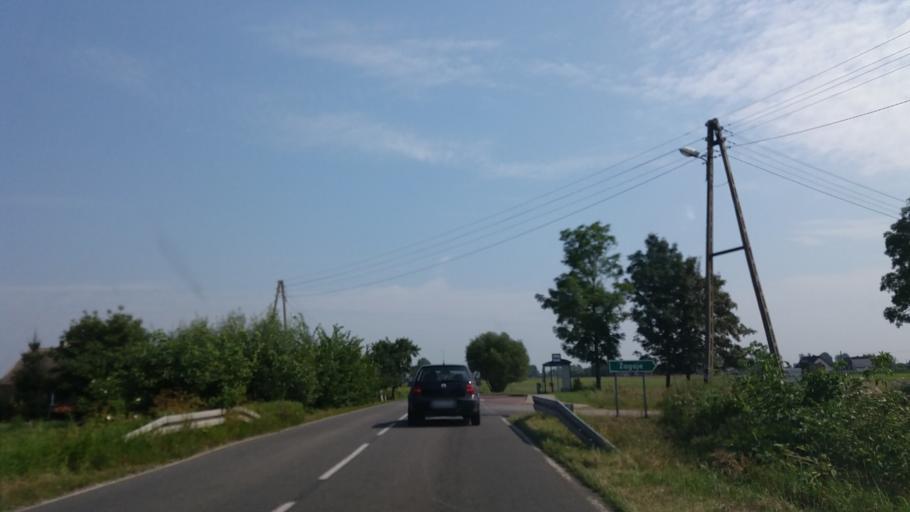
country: PL
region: Lubusz
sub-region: Powiat strzelecko-drezdenecki
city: Zwierzyn
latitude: 52.8214
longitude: 15.6209
